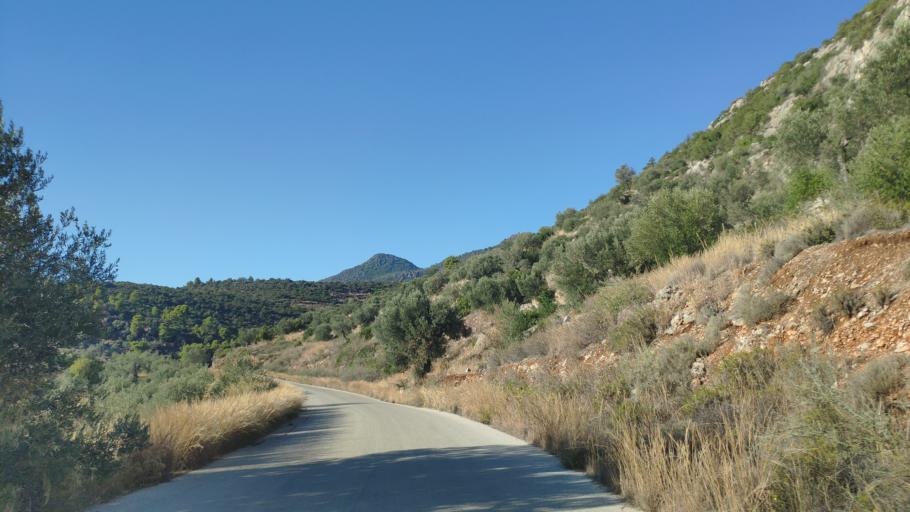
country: GR
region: Attica
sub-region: Nomos Piraios
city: Galatas
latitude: 37.5763
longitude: 23.3600
